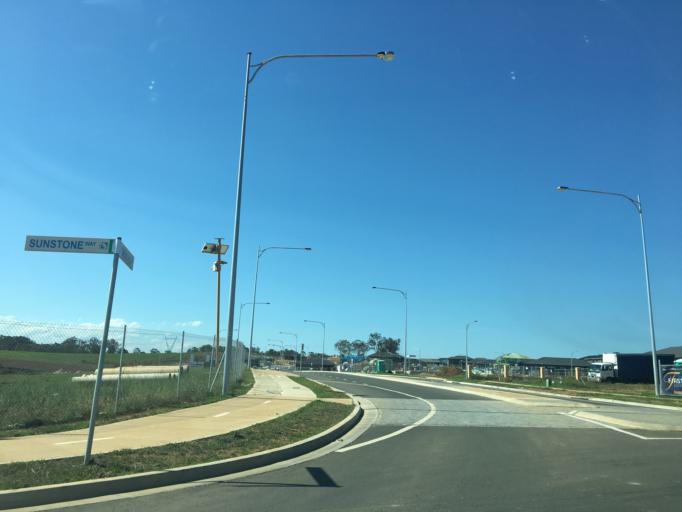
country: AU
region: New South Wales
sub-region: Campbelltown Municipality
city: Denham Court
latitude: -33.9932
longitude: 150.7946
